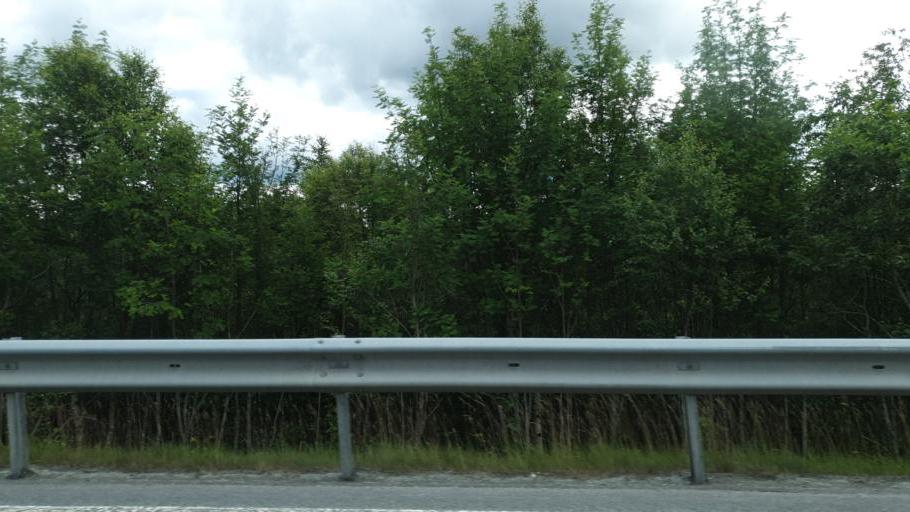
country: NO
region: Sor-Trondelag
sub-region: Rennebu
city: Berkak
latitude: 62.8847
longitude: 10.0997
